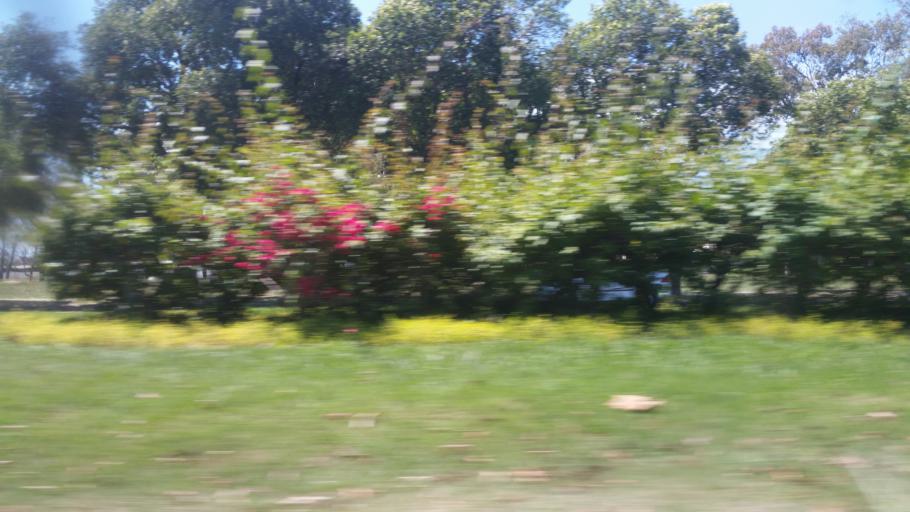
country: BR
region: Rio de Janeiro
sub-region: Rio De Janeiro
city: Rio de Janeiro
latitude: -22.8604
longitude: -43.2275
